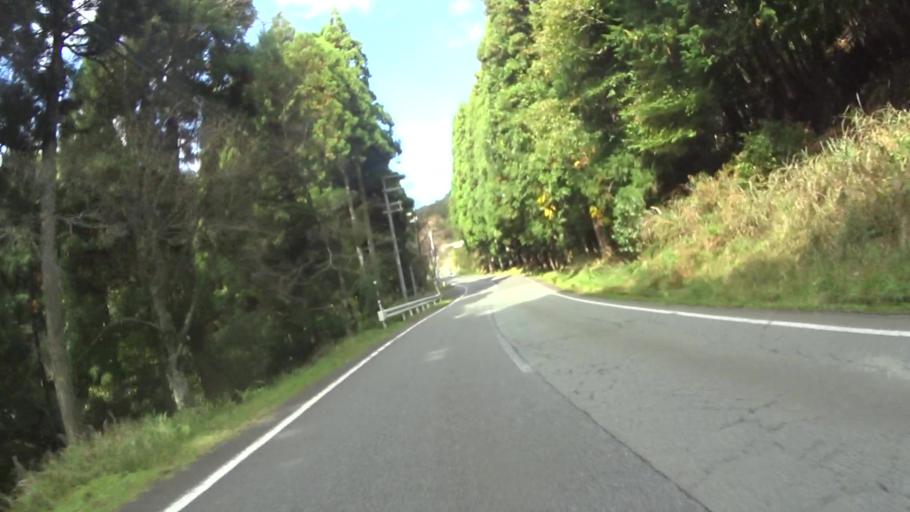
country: JP
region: Hyogo
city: Toyooka
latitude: 35.5145
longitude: 134.9905
